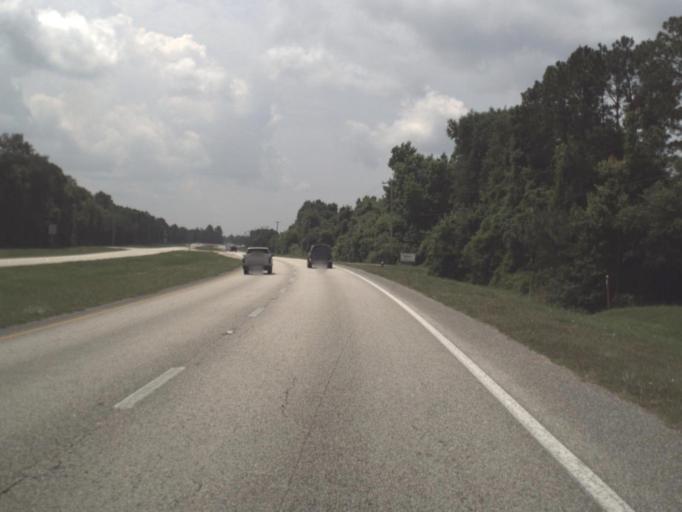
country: US
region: Florida
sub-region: Clay County
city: Green Cove Springs
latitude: 29.9698
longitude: -81.6759
